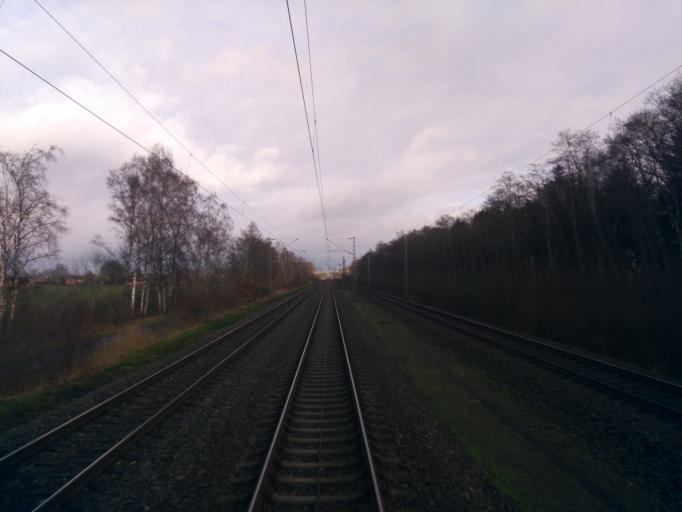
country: DE
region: Lower Saxony
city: Vahlde
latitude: 53.2275
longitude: 9.6357
